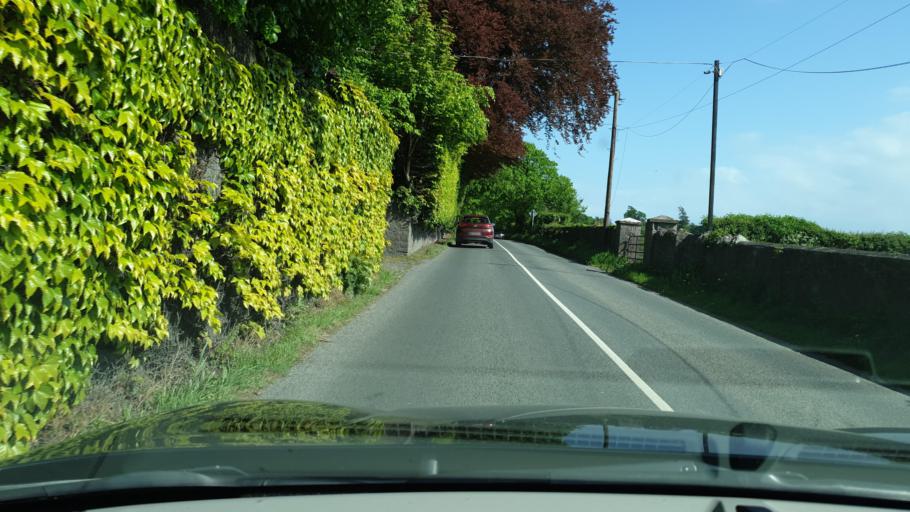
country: IE
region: Leinster
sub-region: Kildare
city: Maynooth
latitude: 53.3945
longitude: -6.5803
